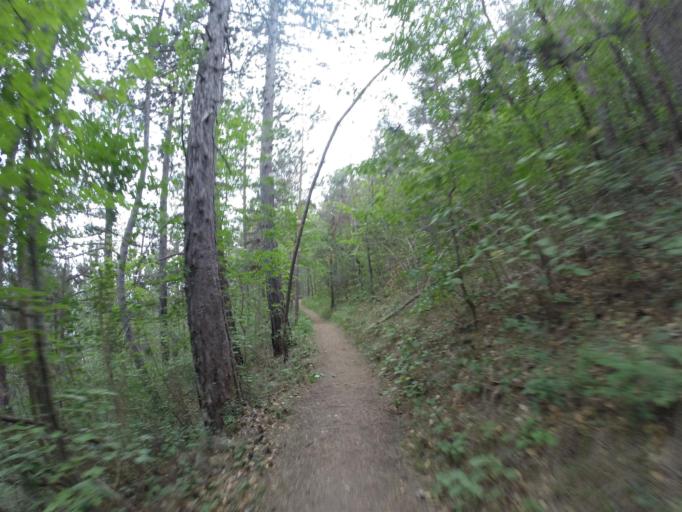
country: DE
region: Thuringia
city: Sulza
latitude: 50.8969
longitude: 11.6217
